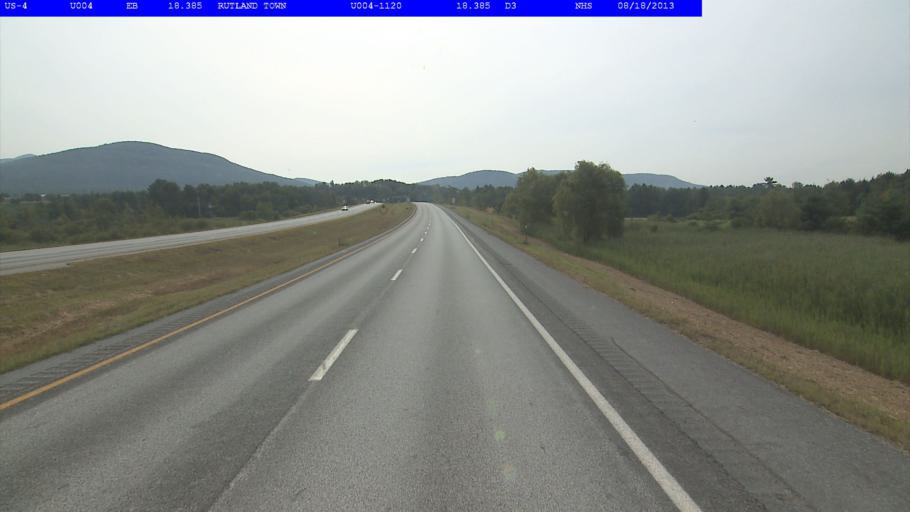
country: US
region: Vermont
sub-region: Rutland County
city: Rutland
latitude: 43.5807
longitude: -72.9750
